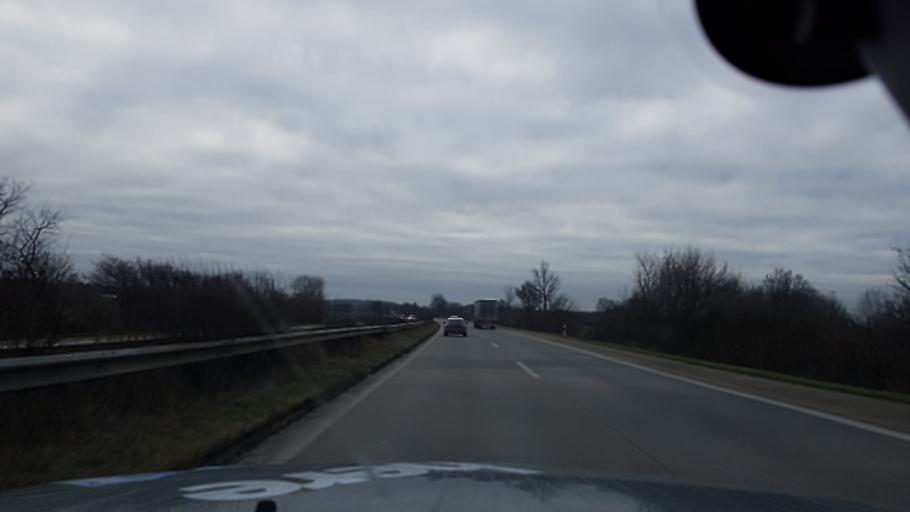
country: DE
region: Schleswig-Holstein
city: Ratekau
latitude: 53.9740
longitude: 10.7327
